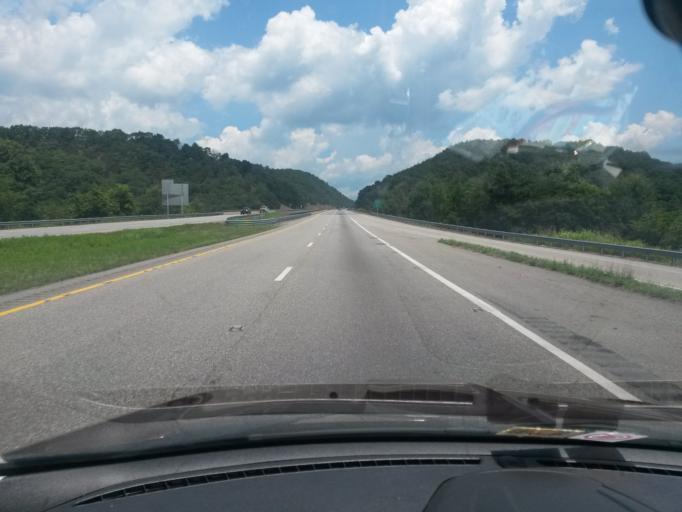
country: US
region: Virginia
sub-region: Alleghany County
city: Clifton Forge
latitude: 37.8118
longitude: -79.8472
